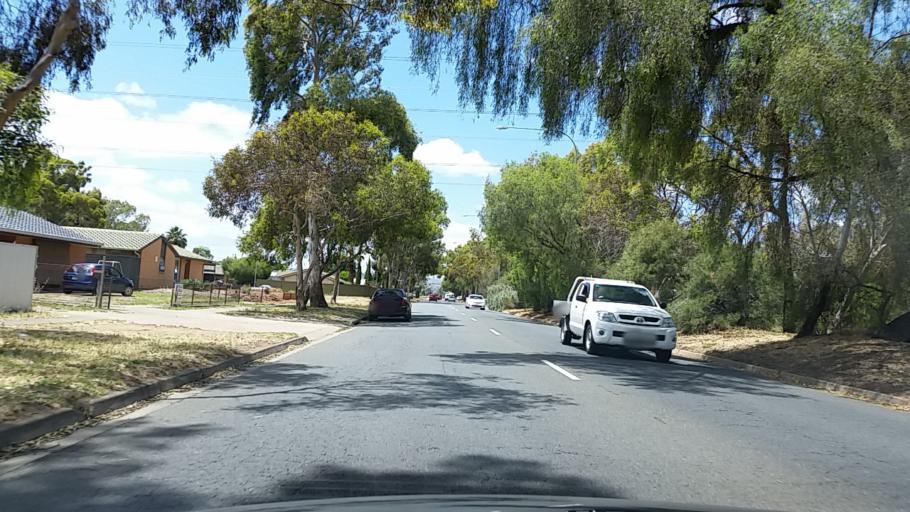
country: AU
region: South Australia
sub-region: Salisbury
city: Salisbury
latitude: -34.7685
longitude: 138.6088
